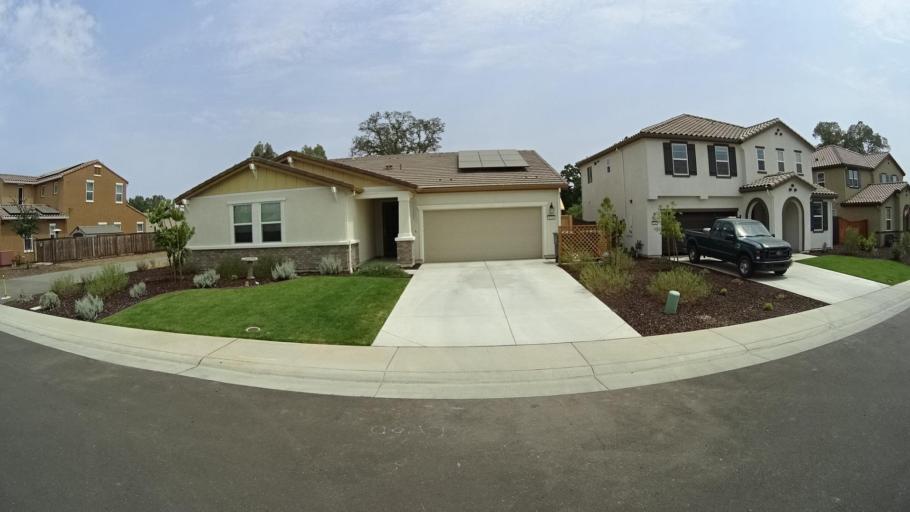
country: US
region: California
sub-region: Placer County
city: Loomis
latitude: 38.8058
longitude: -121.1973
